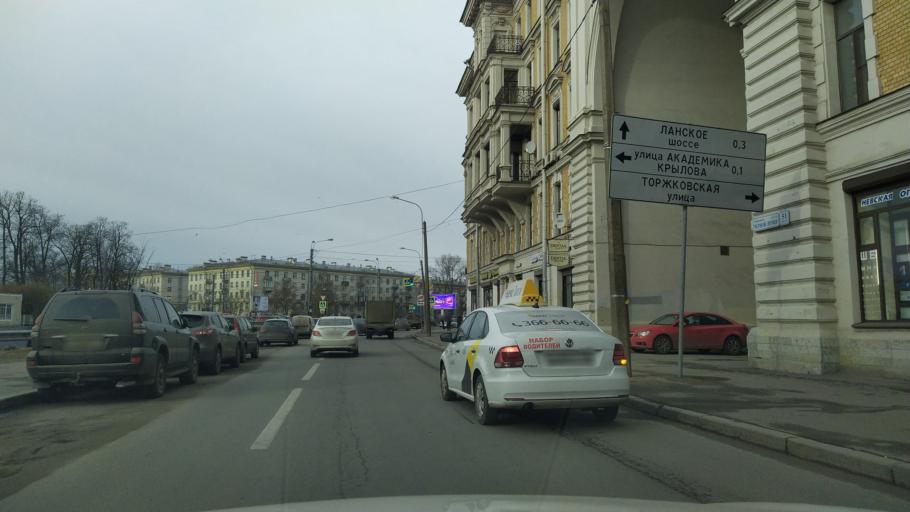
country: RU
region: Leningrad
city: Chernaya Rechka
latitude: 59.9858
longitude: 30.3044
